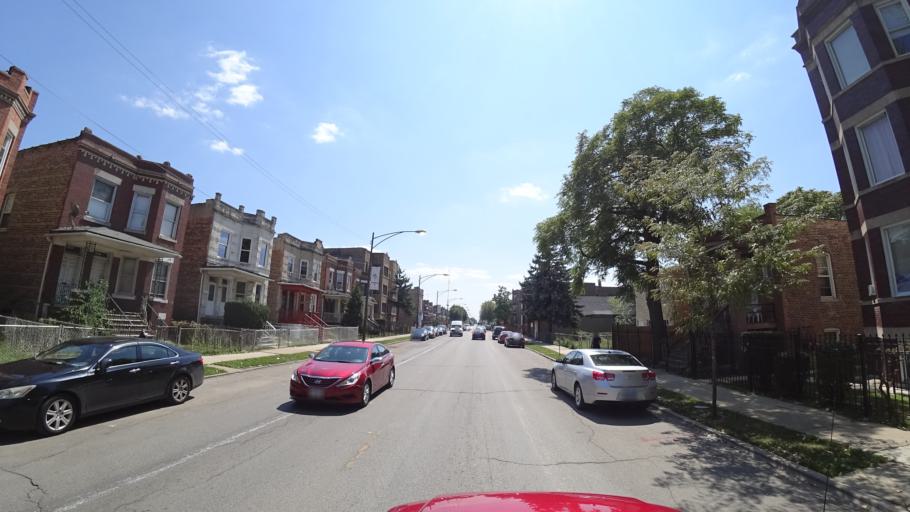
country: US
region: Illinois
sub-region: Cook County
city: Cicero
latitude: 41.8614
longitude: -87.7348
